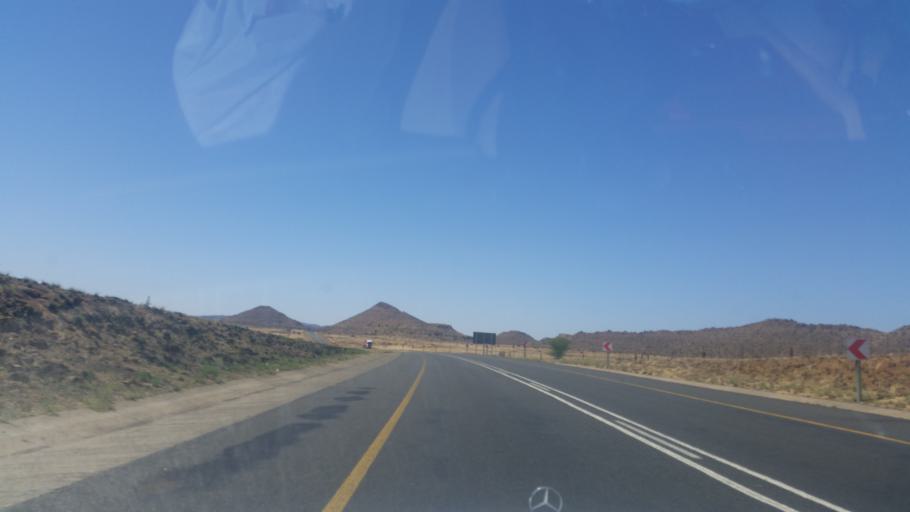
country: ZA
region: Northern Cape
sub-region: Pixley ka Seme District Municipality
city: Colesberg
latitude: -30.6102
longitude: 25.3829
